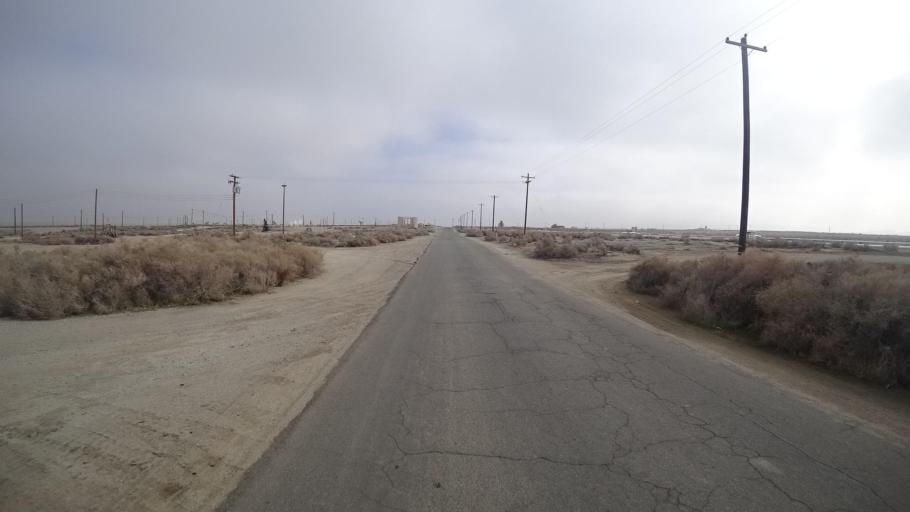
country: US
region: California
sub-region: Kern County
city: Maricopa
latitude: 35.0346
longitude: -119.3526
